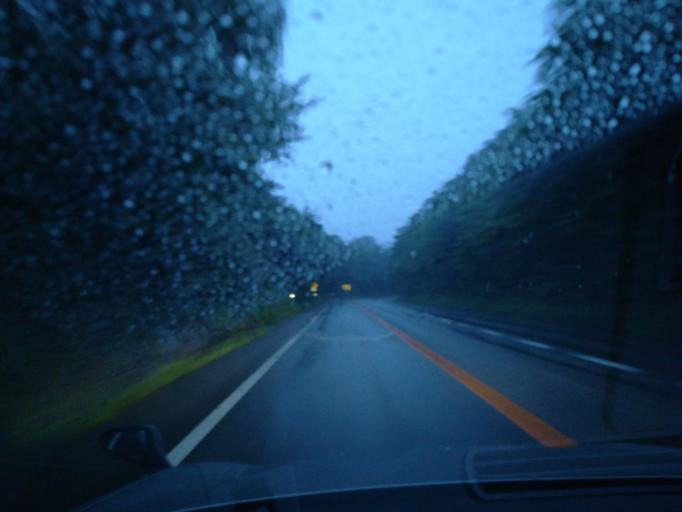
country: JP
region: Nagano
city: Saku
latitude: 36.3061
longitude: 138.6586
